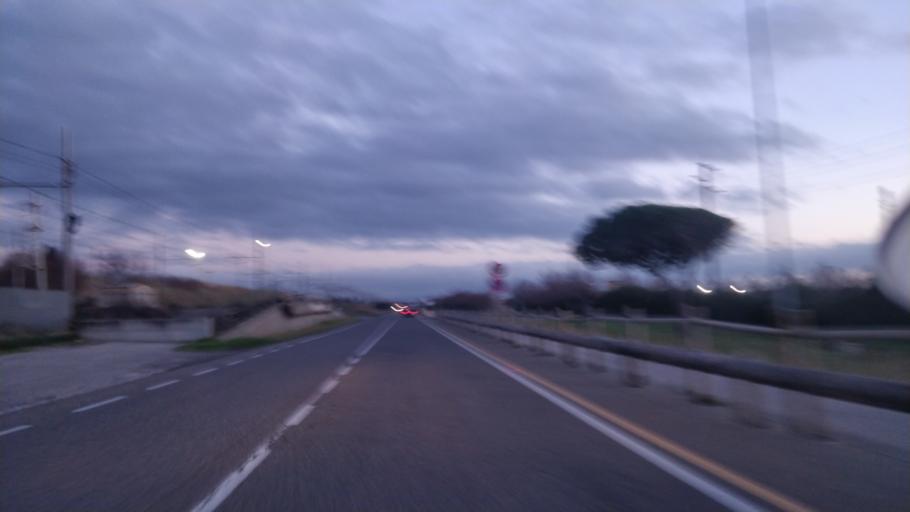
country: IT
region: Tuscany
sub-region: Provincia di Livorno
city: Rosignano Solvay-Castiglioncello
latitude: 43.3808
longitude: 10.4435
